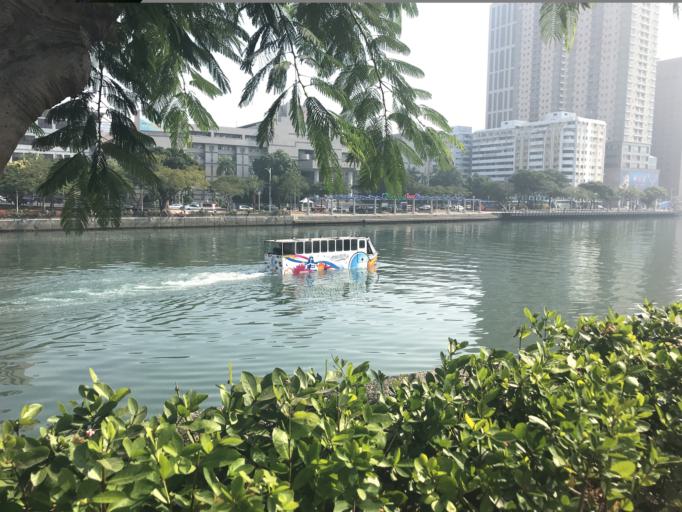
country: TW
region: Kaohsiung
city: Kaohsiung
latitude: 22.6264
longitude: 120.2880
